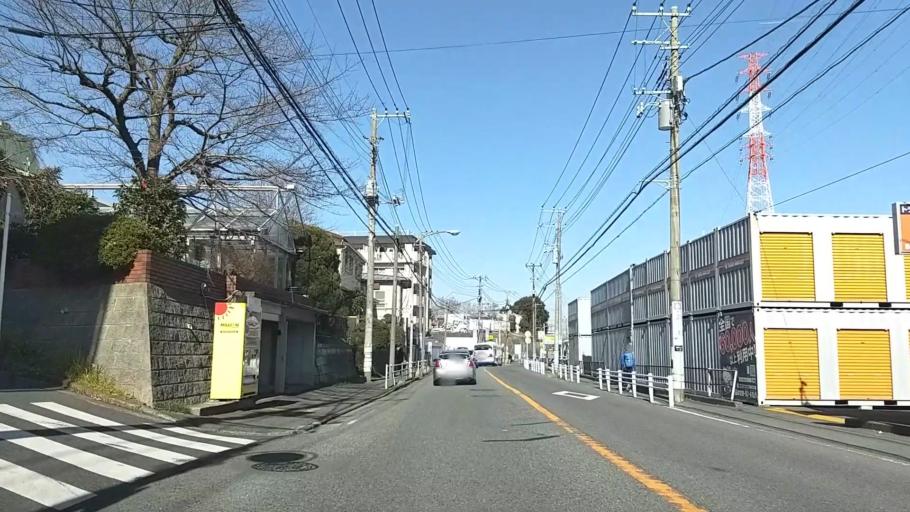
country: JP
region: Kanagawa
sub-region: Kawasaki-shi
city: Kawasaki
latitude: 35.5196
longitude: 139.6498
